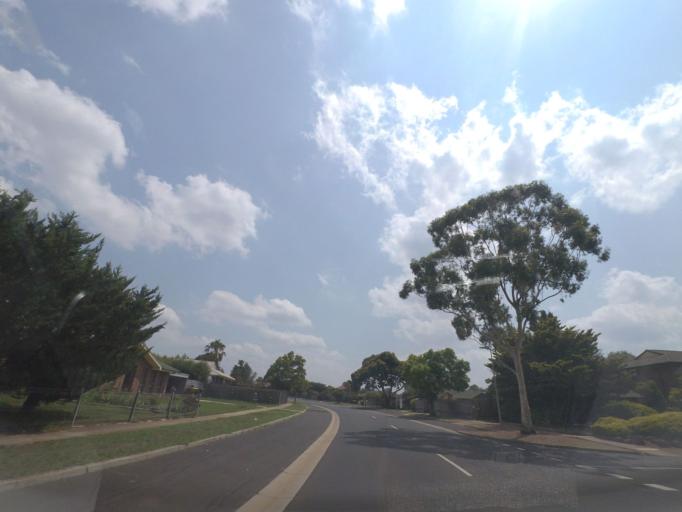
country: AU
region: Victoria
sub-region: Melton
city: Melton West
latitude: -37.6804
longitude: 144.5629
